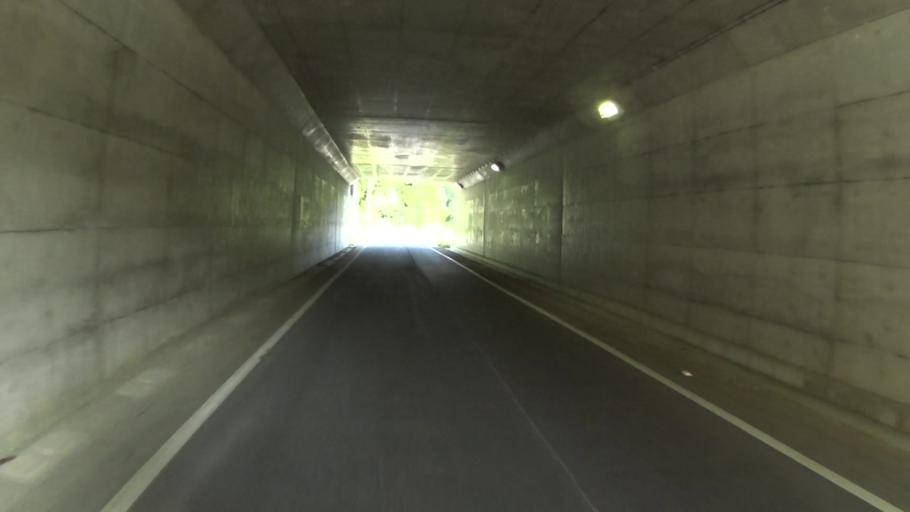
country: JP
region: Kyoto
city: Miyazu
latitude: 35.5674
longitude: 135.1204
